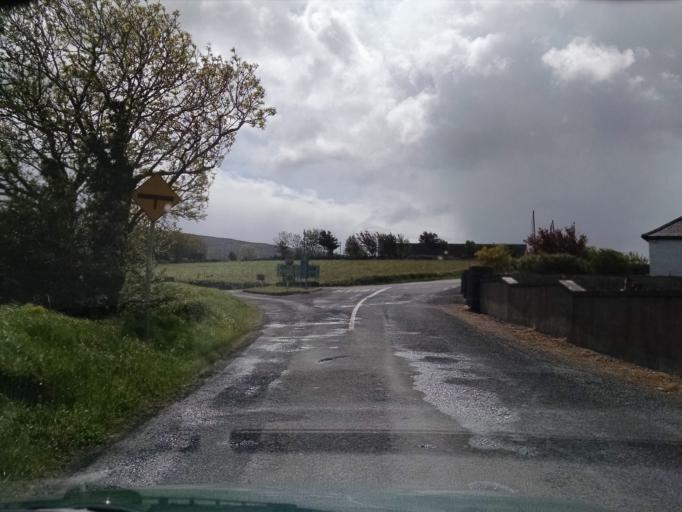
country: IE
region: Connaught
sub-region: County Galway
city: Bearna
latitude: 53.1471
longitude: -9.0808
